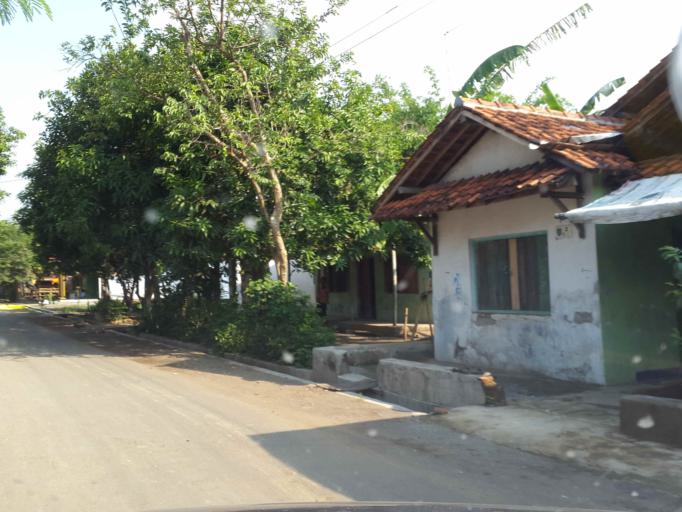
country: ID
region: Central Java
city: Balapulang
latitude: -7.0015
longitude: 109.0842
